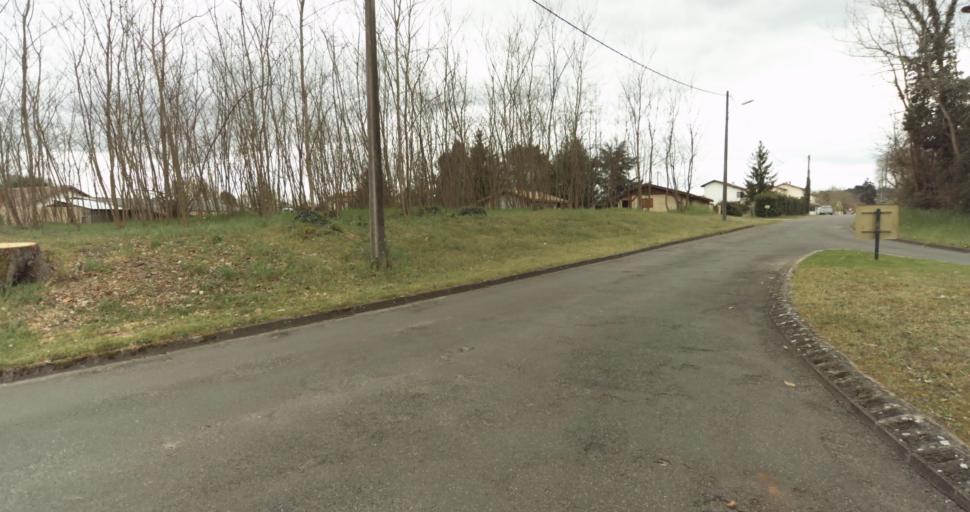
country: FR
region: Aquitaine
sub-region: Departement des Landes
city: Roquefort
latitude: 44.0360
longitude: -0.3174
